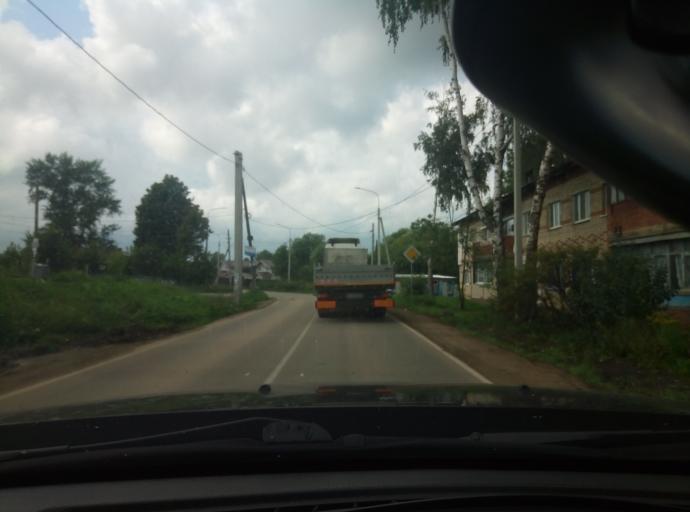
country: RU
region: Tula
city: Borodinskiy
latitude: 53.9995
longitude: 37.8162
